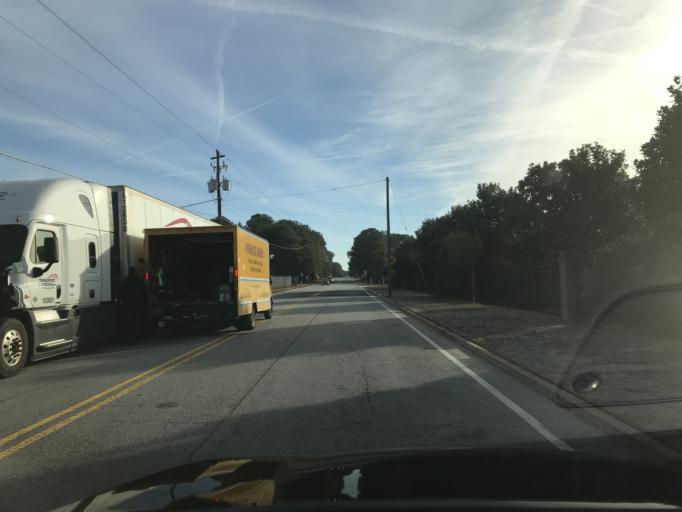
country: US
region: Georgia
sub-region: Clayton County
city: Morrow
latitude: 33.5642
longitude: -84.3573
